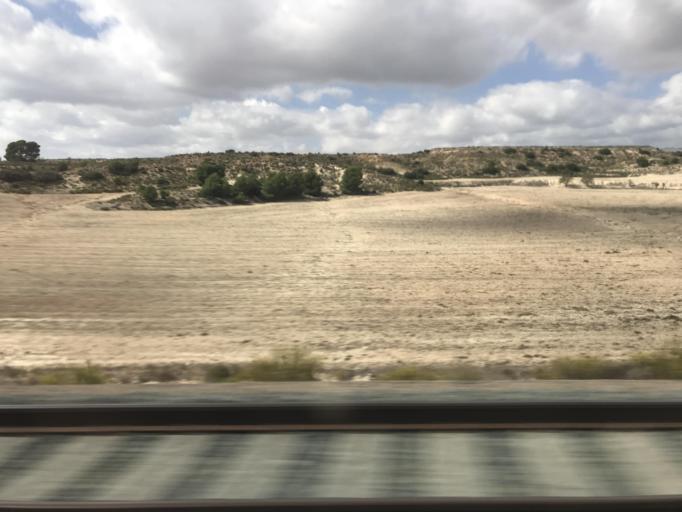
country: ES
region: Castille-La Mancha
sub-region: Provincia de Albacete
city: Caudete
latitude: 38.7178
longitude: -0.9318
